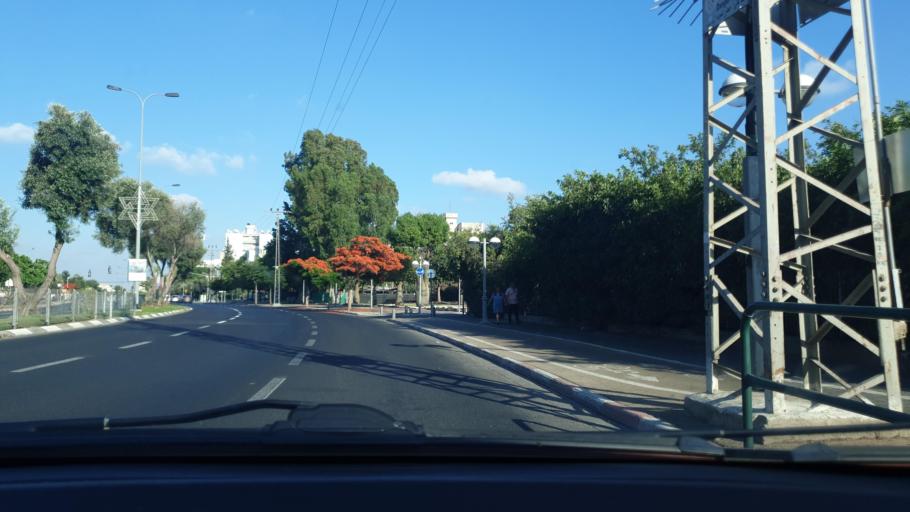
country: IL
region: Tel Aviv
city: Giv`atayim
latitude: 32.0572
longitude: 34.8048
